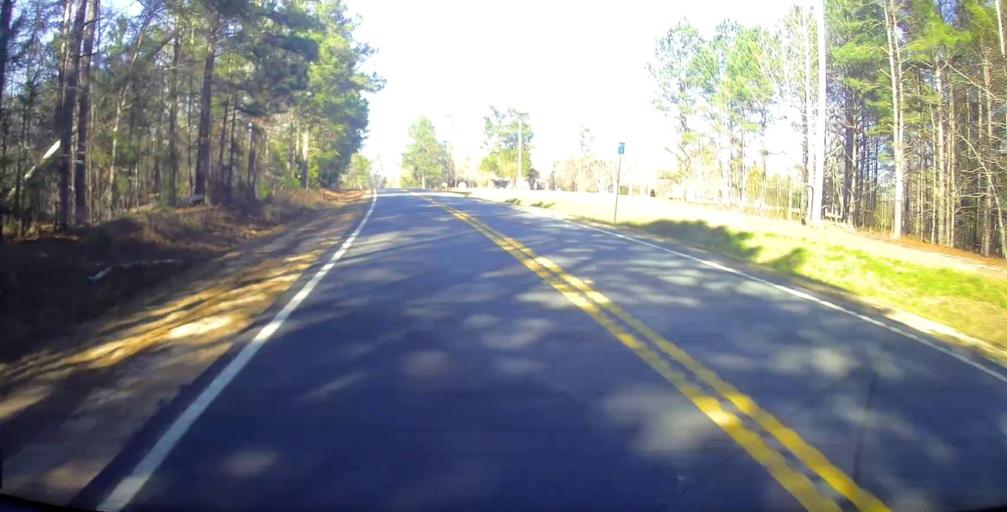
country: US
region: Georgia
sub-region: Taylor County
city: Butler
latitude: 32.6571
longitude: -84.3643
